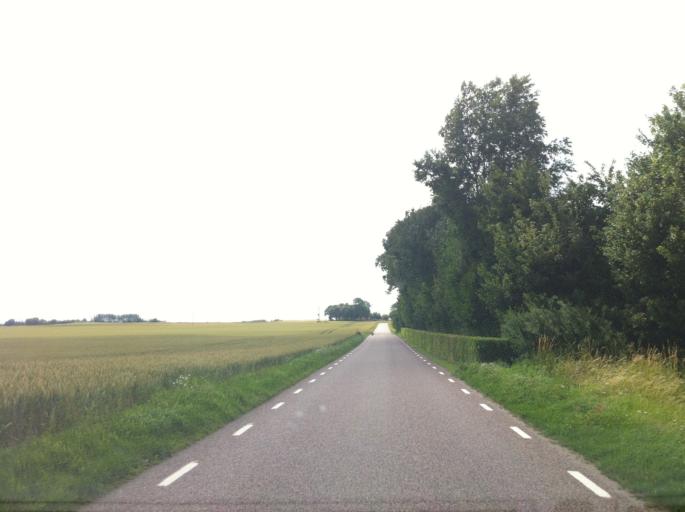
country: SE
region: Skane
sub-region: Skurups Kommun
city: Skurup
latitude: 55.4281
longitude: 13.4516
